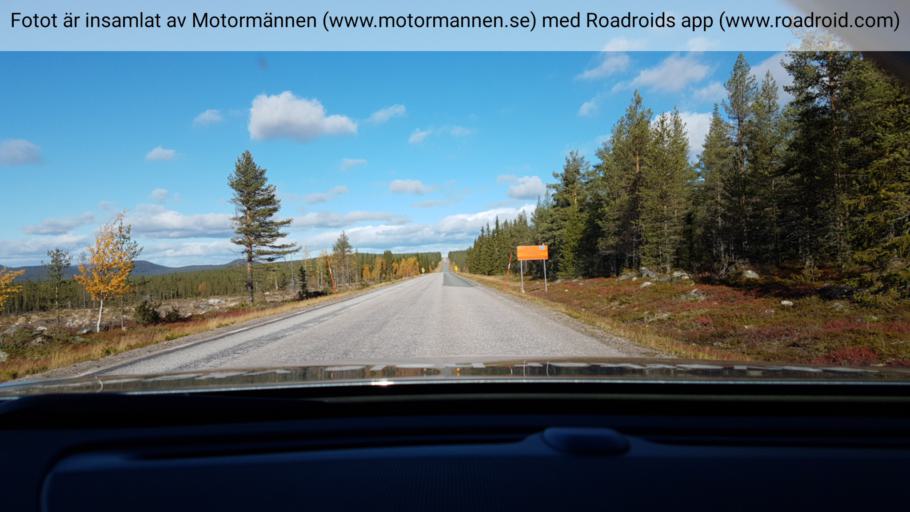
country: SE
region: Norrbotten
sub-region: Arjeplogs Kommun
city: Arjeplog
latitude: 65.8175
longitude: 18.4440
